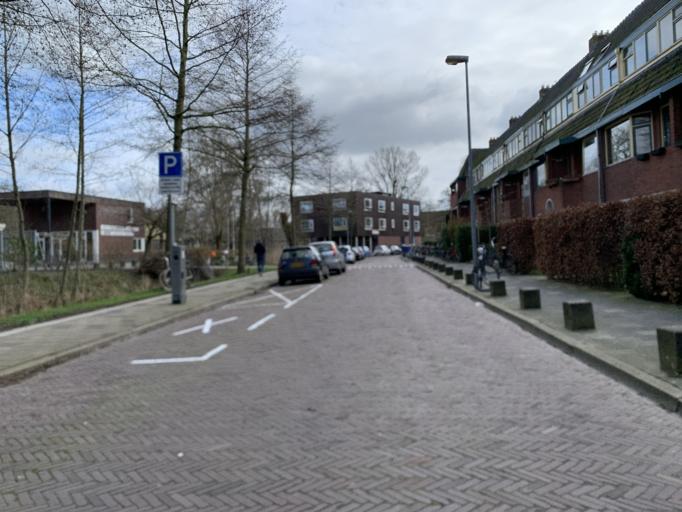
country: NL
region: Groningen
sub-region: Gemeente Groningen
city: Korrewegwijk
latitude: 53.2339
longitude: 6.5729
